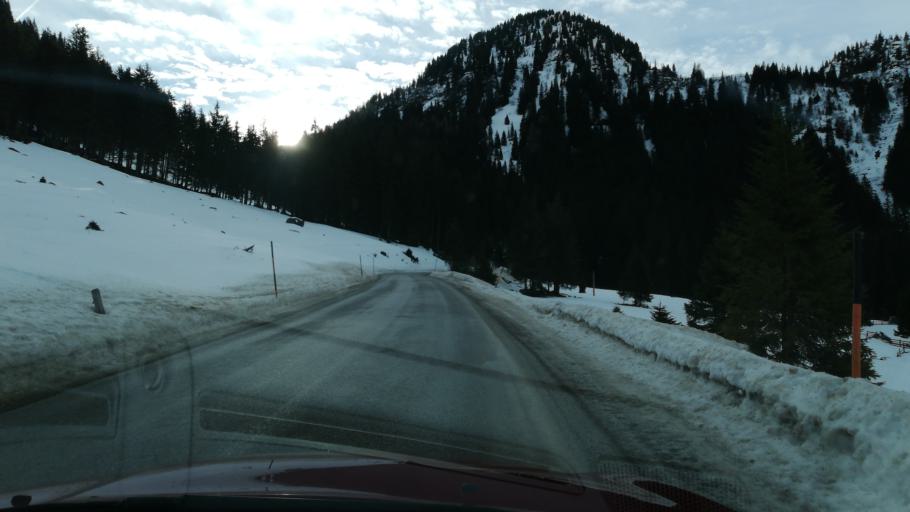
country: AT
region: Styria
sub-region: Politischer Bezirk Liezen
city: Donnersbach
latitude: 47.4130
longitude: 14.1791
